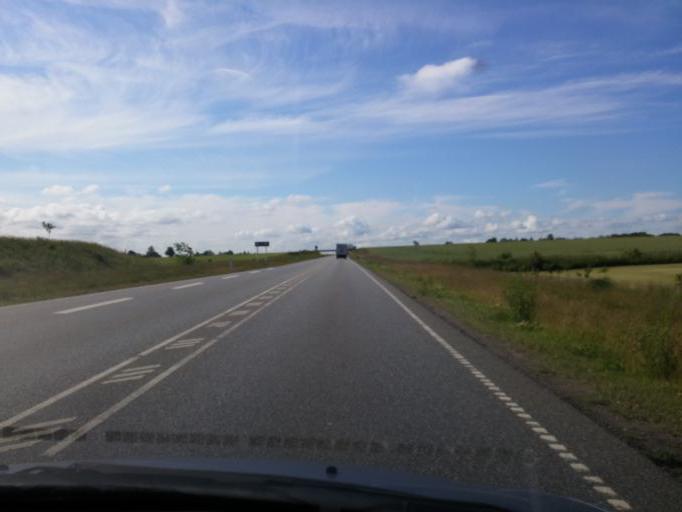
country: DK
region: South Denmark
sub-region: Odense Kommune
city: Bullerup
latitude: 55.4038
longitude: 10.4738
